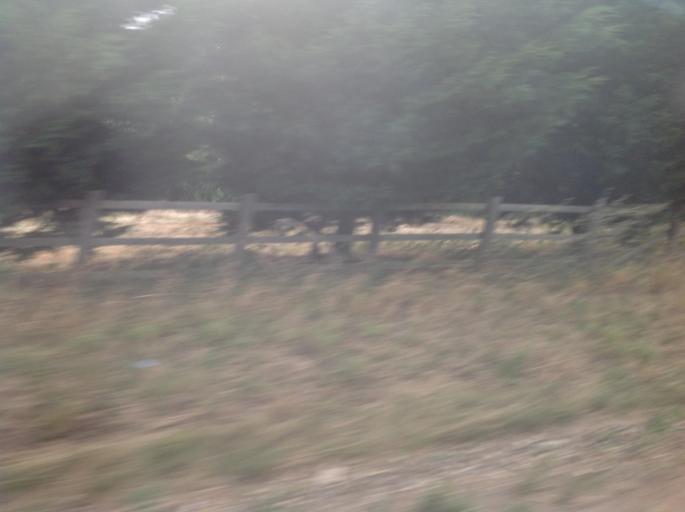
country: GB
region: England
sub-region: Suffolk
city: Shotley Gate
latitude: 52.0080
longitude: 1.2826
